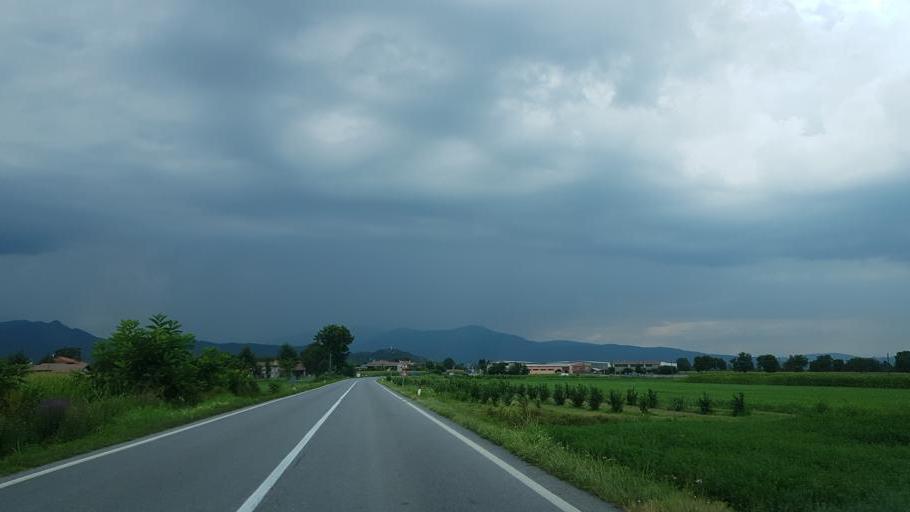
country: IT
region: Piedmont
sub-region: Provincia di Cuneo
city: Bernezzo
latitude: 44.3980
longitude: 7.4513
